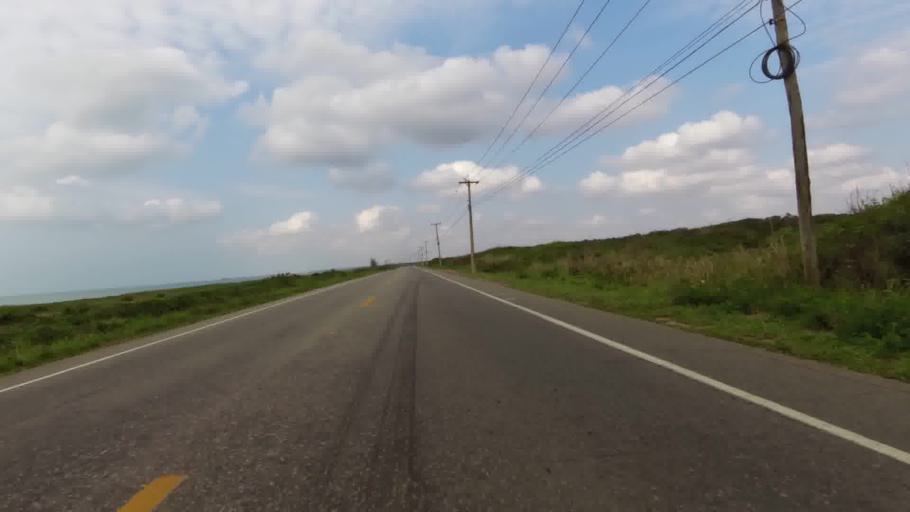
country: BR
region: Espirito Santo
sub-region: Itapemirim
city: Itapemirim
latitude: -20.9413
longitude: -40.8040
